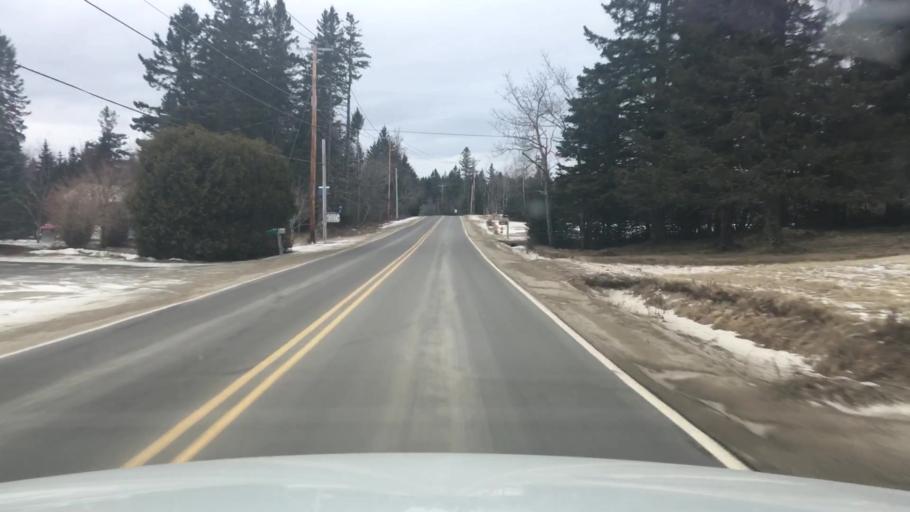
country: US
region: Maine
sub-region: Washington County
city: Addison
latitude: 44.6229
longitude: -67.7118
